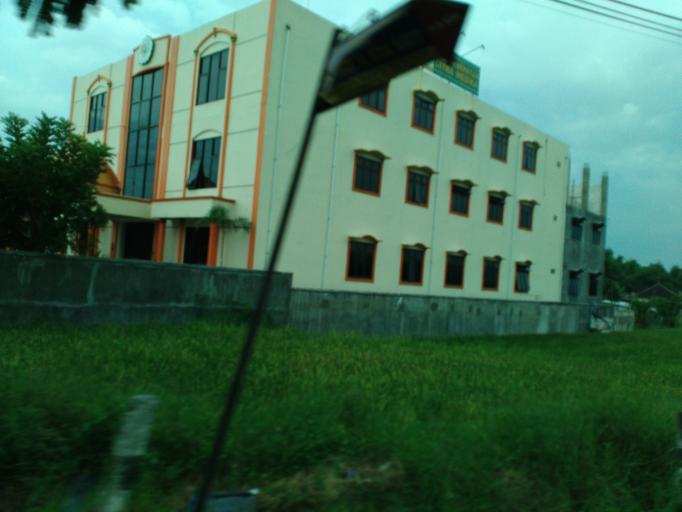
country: ID
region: Central Java
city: Gatak
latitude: -7.5915
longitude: 110.7041
